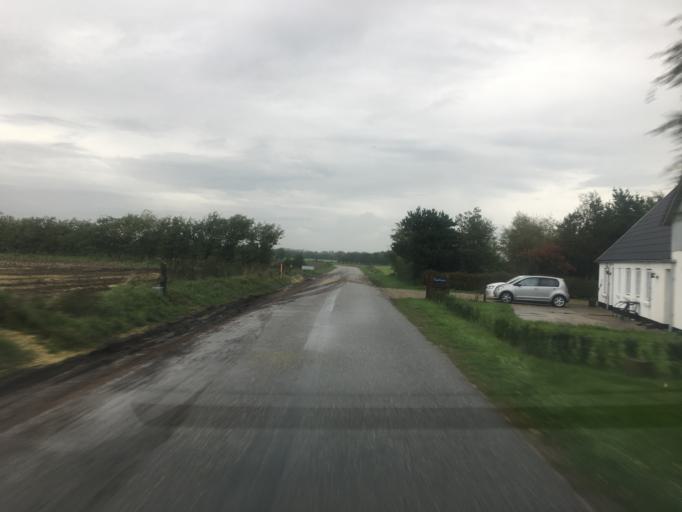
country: DK
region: South Denmark
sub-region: Tonder Kommune
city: Logumkloster
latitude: 55.0105
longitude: 9.0334
